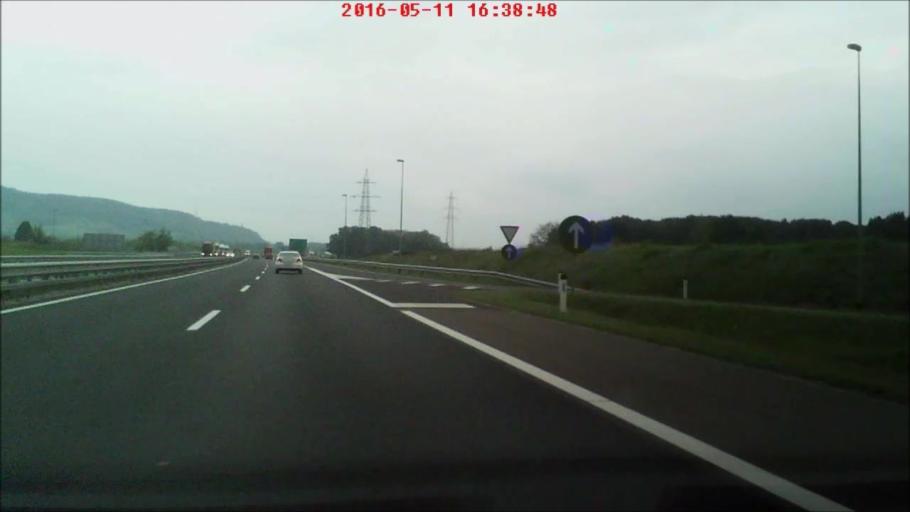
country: SI
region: Miklavz na Dravskem Polju
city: Miklavz na Dravskem Polju
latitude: 46.5465
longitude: 15.6940
